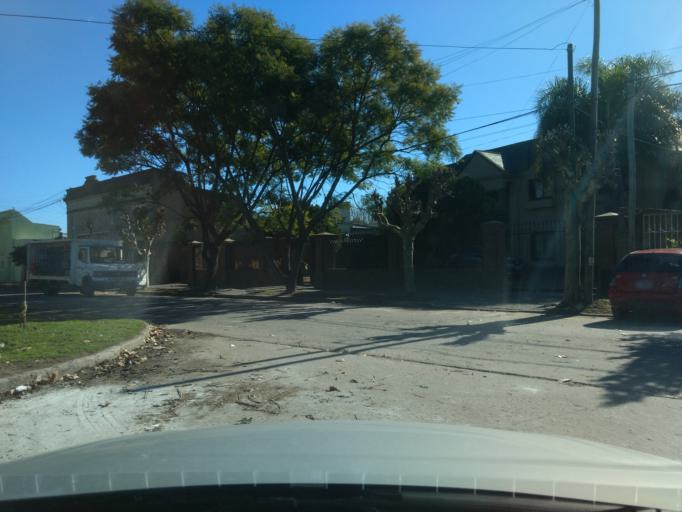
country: AR
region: Buenos Aires
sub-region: Partido de Lujan
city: Lujan
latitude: -34.5769
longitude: -59.1048
